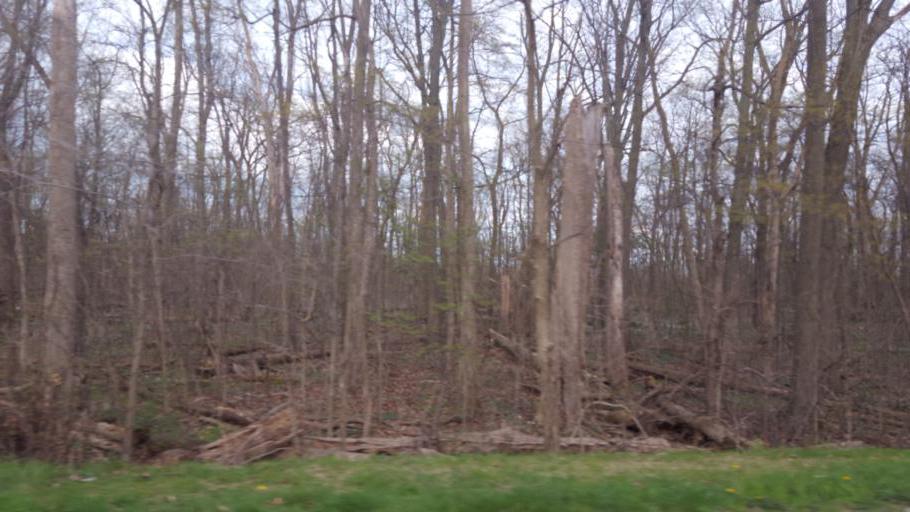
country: US
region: Ohio
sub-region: Erie County
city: Sandusky
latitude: 41.5101
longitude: -82.7617
